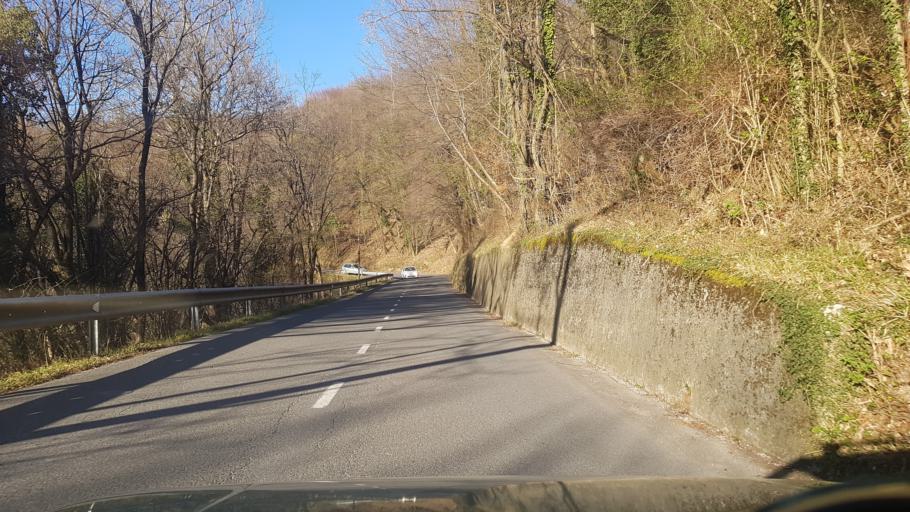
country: IT
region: Friuli Venezia Giulia
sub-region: Provincia di Gorizia
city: San Floriano del Collio
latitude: 46.0165
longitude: 13.5749
